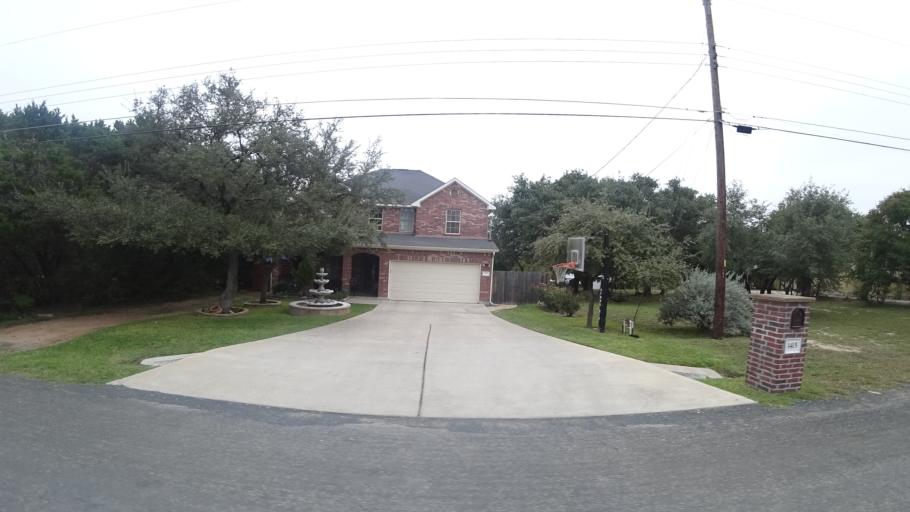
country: US
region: Texas
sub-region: Travis County
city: Hudson Bend
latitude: 30.3724
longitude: -97.9339
